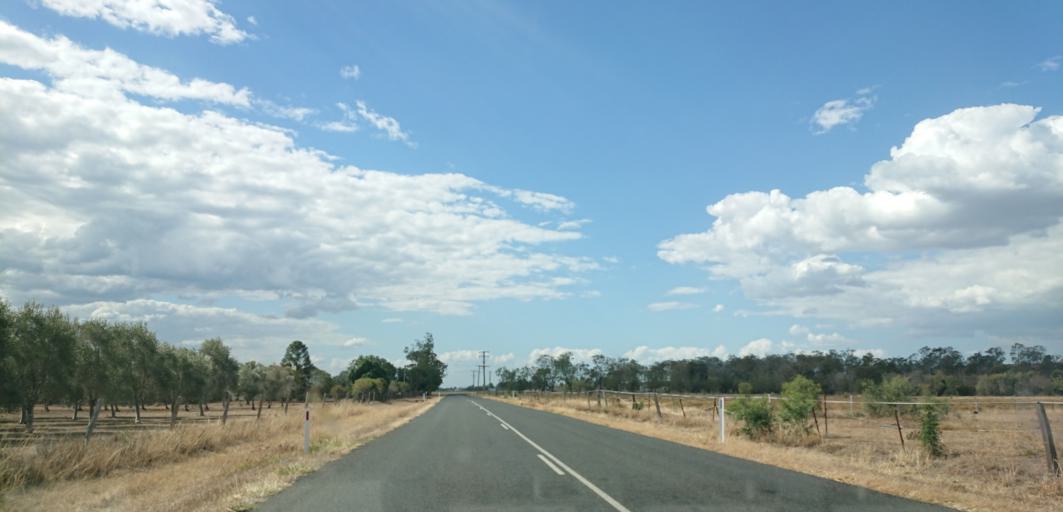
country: AU
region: Queensland
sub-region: Lockyer Valley
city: Gatton
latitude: -27.6247
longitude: 152.1999
